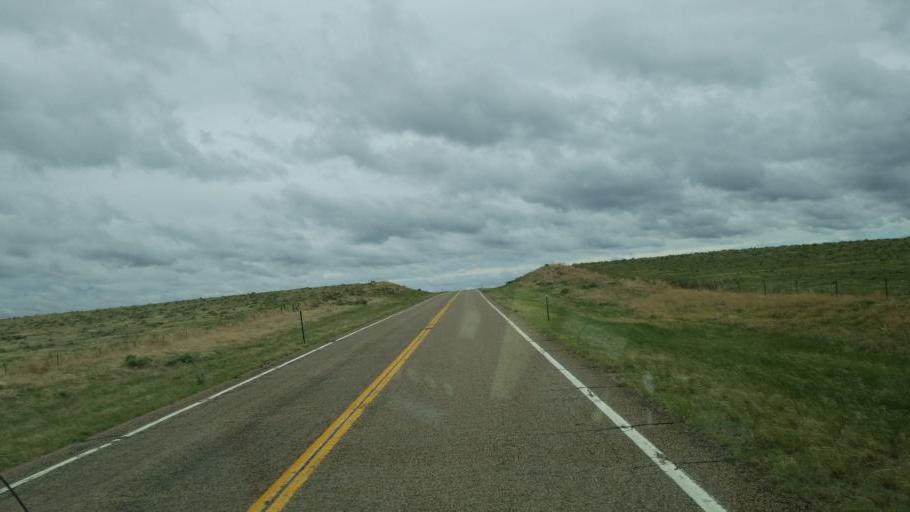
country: US
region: Colorado
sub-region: Lincoln County
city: Hugo
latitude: 38.8507
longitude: -103.5512
